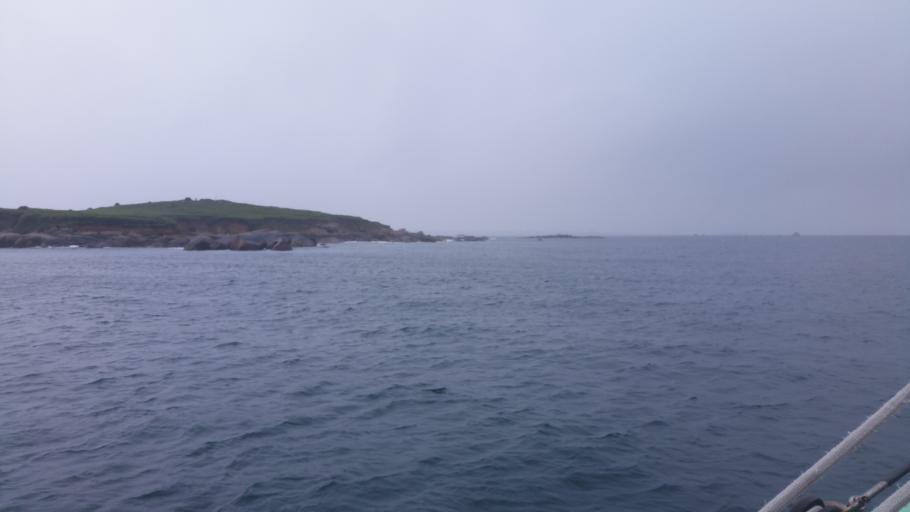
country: FR
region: Brittany
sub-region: Departement du Finistere
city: Carantec
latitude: 48.6976
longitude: -3.9205
